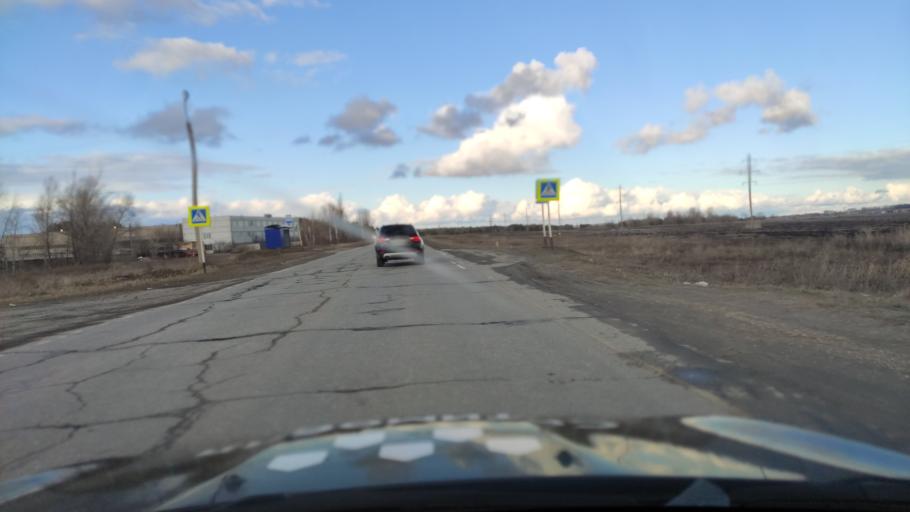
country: RU
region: Samara
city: Povolzhskiy
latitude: 53.5762
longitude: 49.6941
